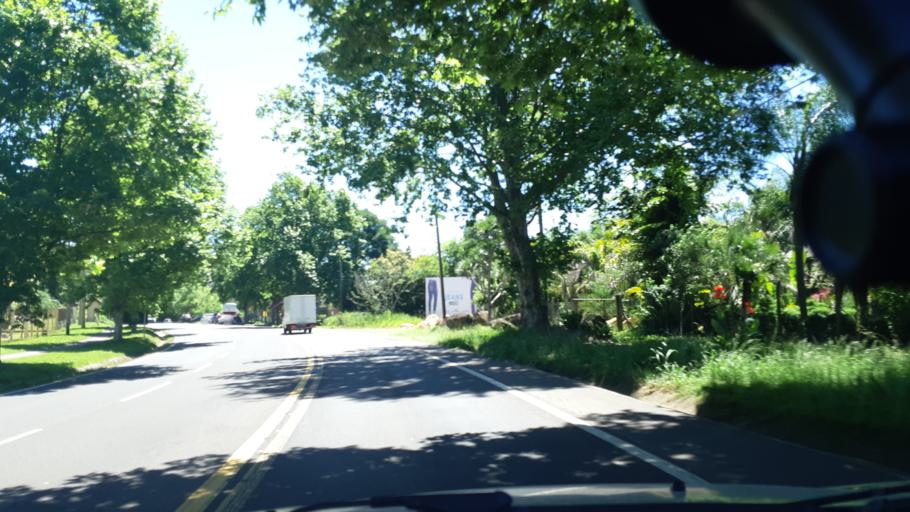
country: BR
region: Rio Grande do Sul
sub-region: Ivoti
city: Ivoti
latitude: -29.6199
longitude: -51.1229
